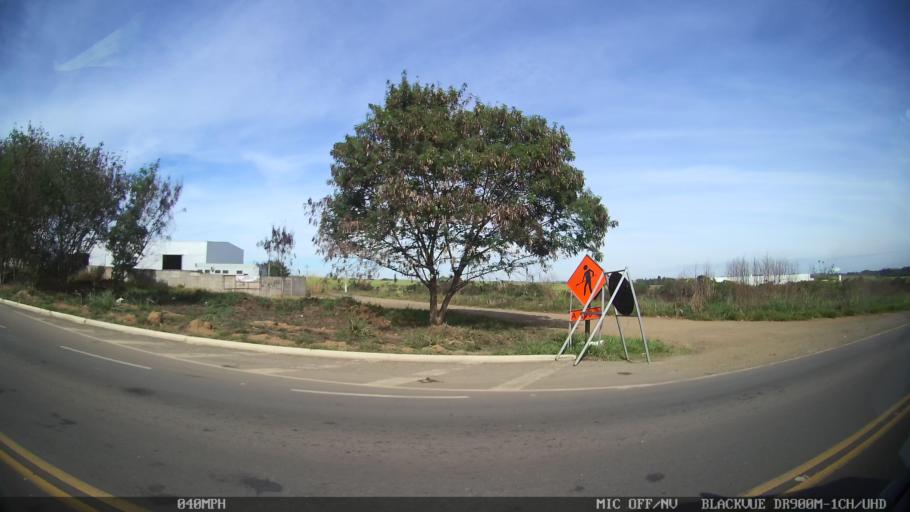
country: BR
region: Sao Paulo
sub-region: Rio Das Pedras
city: Rio das Pedras
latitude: -22.7933
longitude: -47.6205
